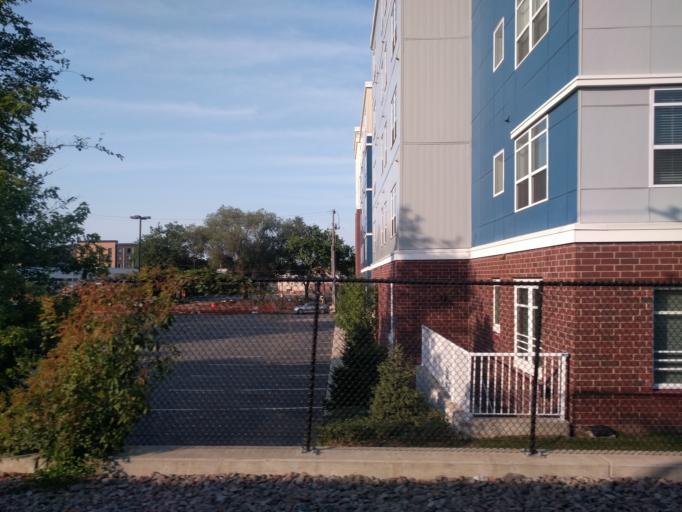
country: US
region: Minnesota
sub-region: Ramsey County
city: Lauderdale
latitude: 44.9733
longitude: -93.2164
